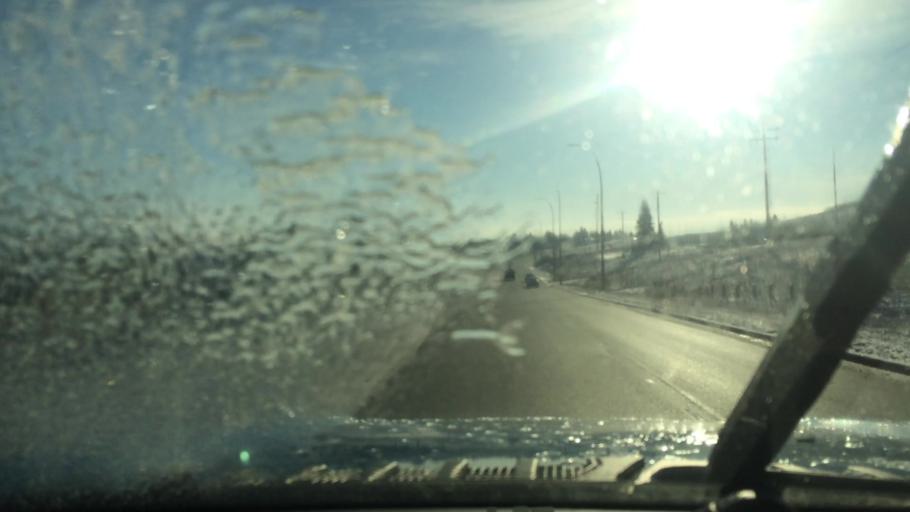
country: CA
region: Alberta
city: Calgary
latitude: 51.1265
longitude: -114.1006
